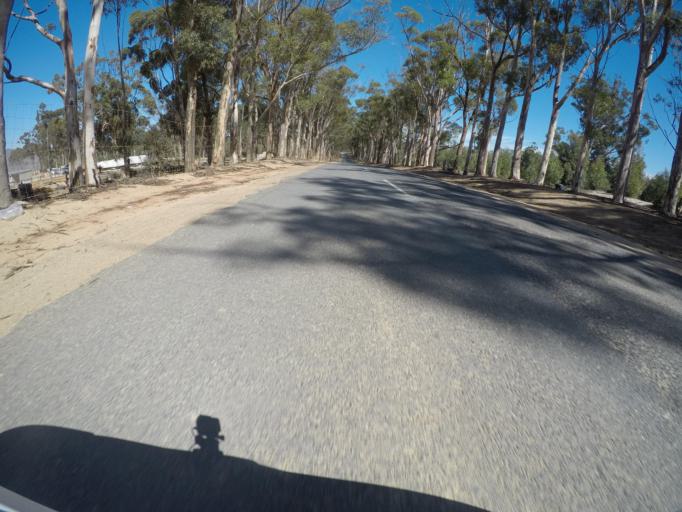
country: ZA
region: Western Cape
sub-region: City of Cape Town
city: Sunset Beach
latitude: -33.7636
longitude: 18.5514
